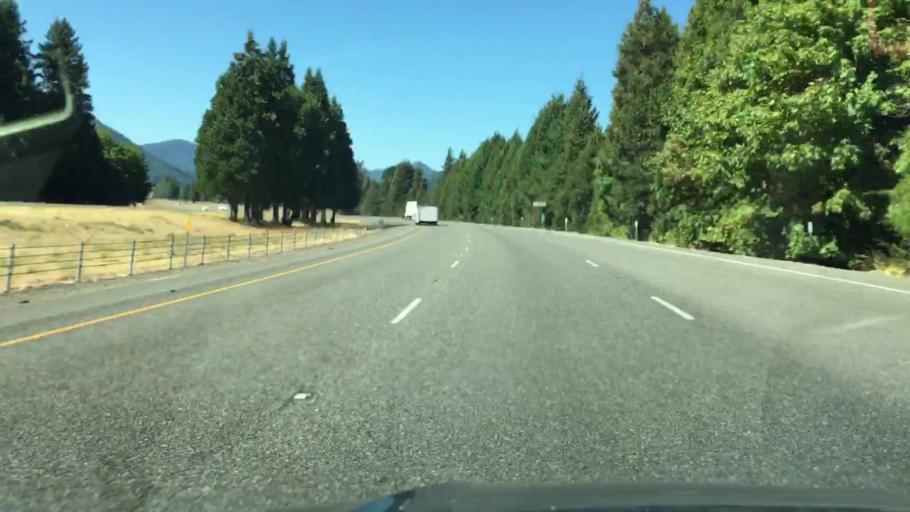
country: US
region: Oregon
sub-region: Douglas County
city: Canyonville
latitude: 42.7673
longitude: -123.3248
